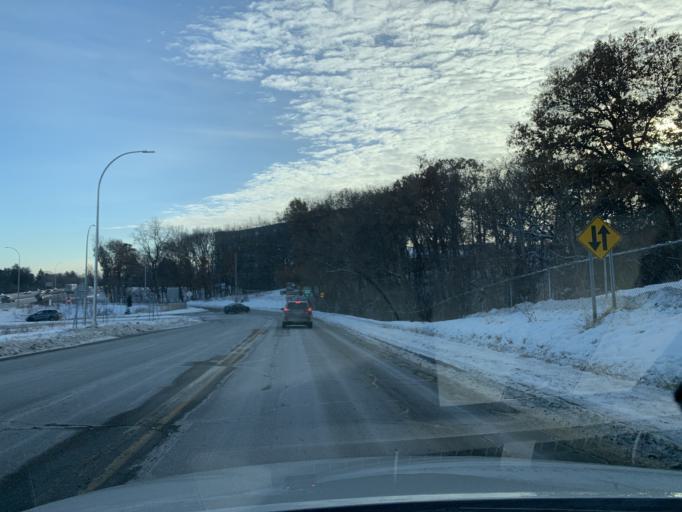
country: US
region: Minnesota
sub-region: Hennepin County
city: Minnetonka Mills
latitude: 44.9539
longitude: -93.4017
